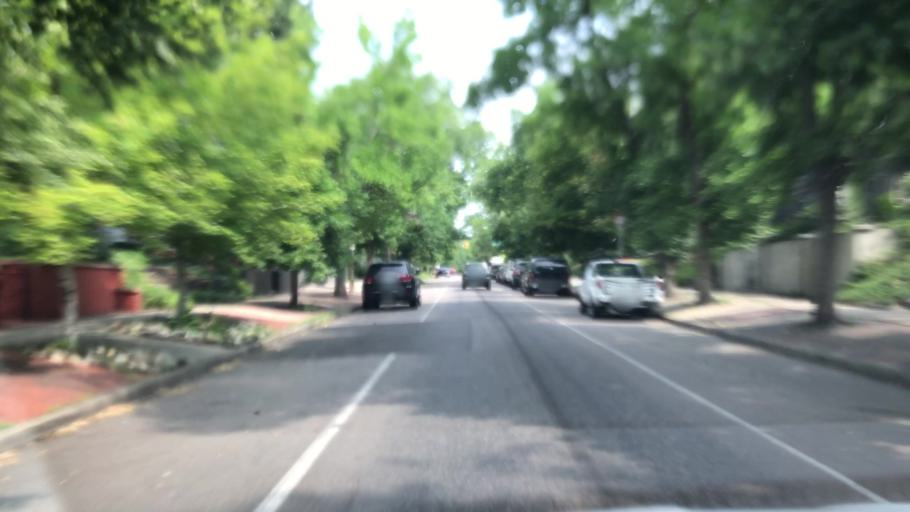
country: US
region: Colorado
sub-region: Denver County
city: Denver
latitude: 39.7278
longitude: -104.9729
